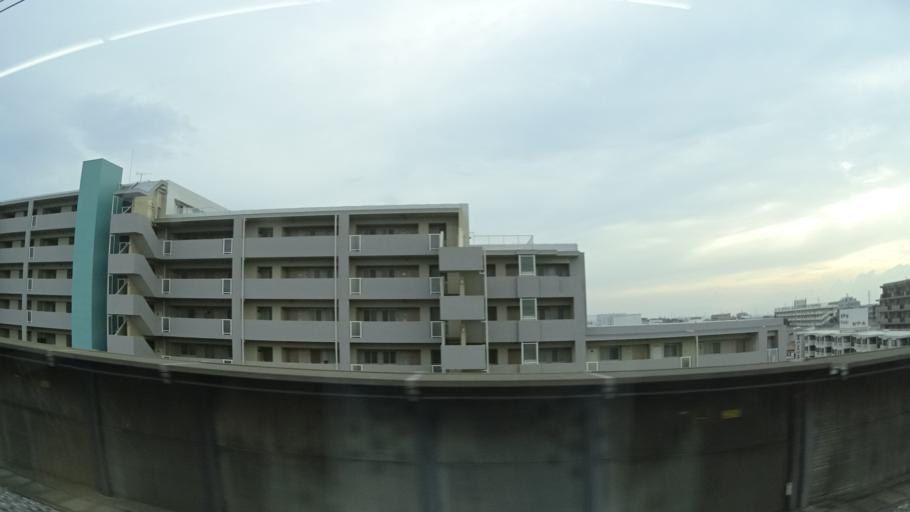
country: JP
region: Saitama
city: Shimotoda
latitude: 35.8353
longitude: 139.6523
